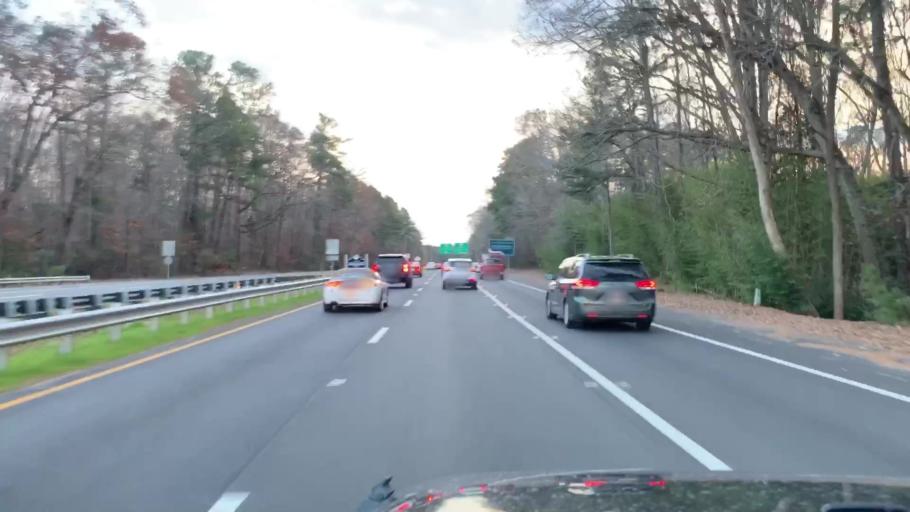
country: US
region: Virginia
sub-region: City of Williamsburg
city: Williamsburg
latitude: 37.3014
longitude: -76.6853
